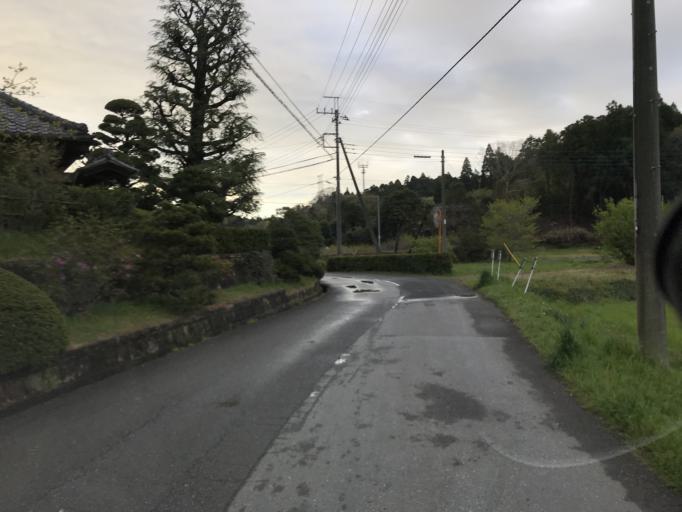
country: JP
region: Chiba
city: Yokaichiba
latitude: 35.7664
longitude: 140.4651
